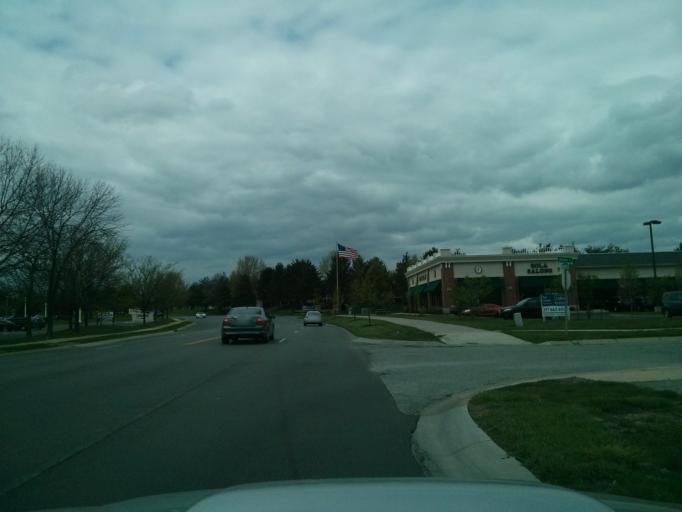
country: US
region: Indiana
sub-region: Hamilton County
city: Carmel
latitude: 39.9678
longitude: -86.1461
